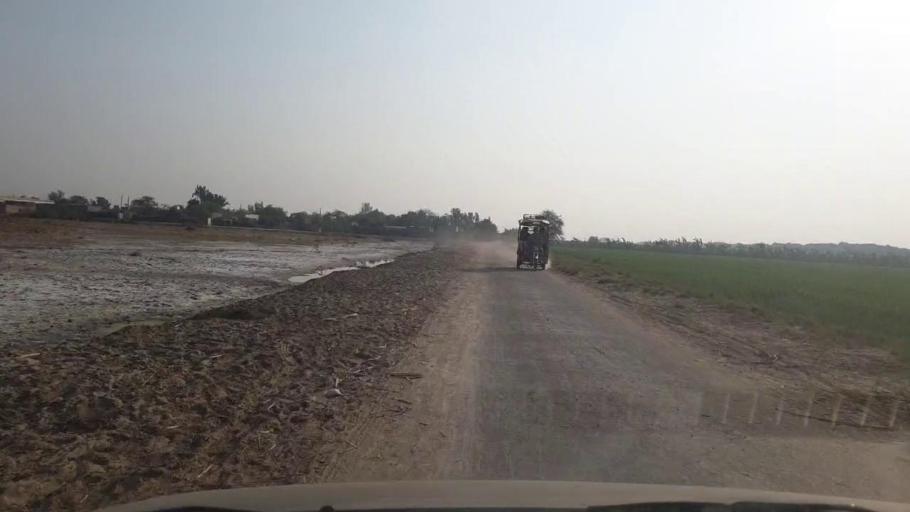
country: PK
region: Sindh
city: Digri
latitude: 25.2548
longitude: 69.1606
